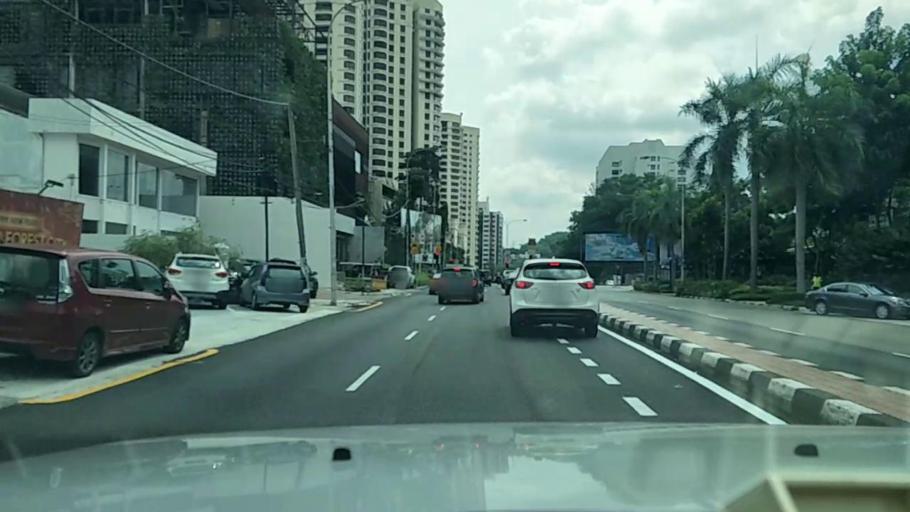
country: MY
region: Kuala Lumpur
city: Kuala Lumpur
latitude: 3.1424
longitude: 101.6677
